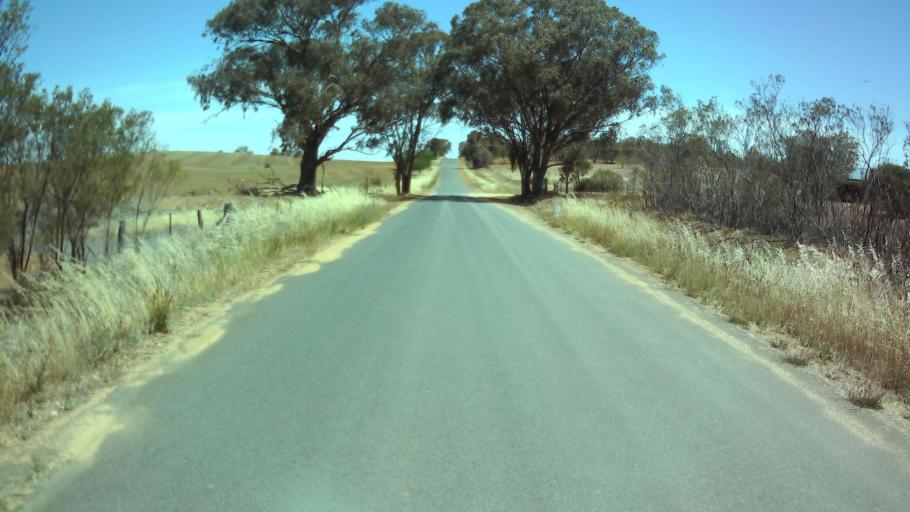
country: AU
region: New South Wales
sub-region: Weddin
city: Grenfell
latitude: -33.8997
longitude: 148.1849
